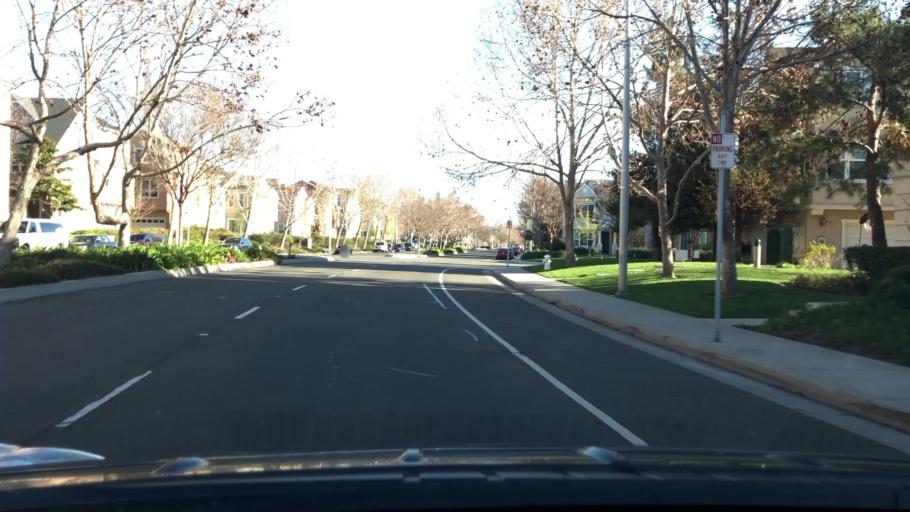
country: US
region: California
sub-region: Santa Clara County
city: Santa Clara
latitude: 37.4010
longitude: -121.9501
